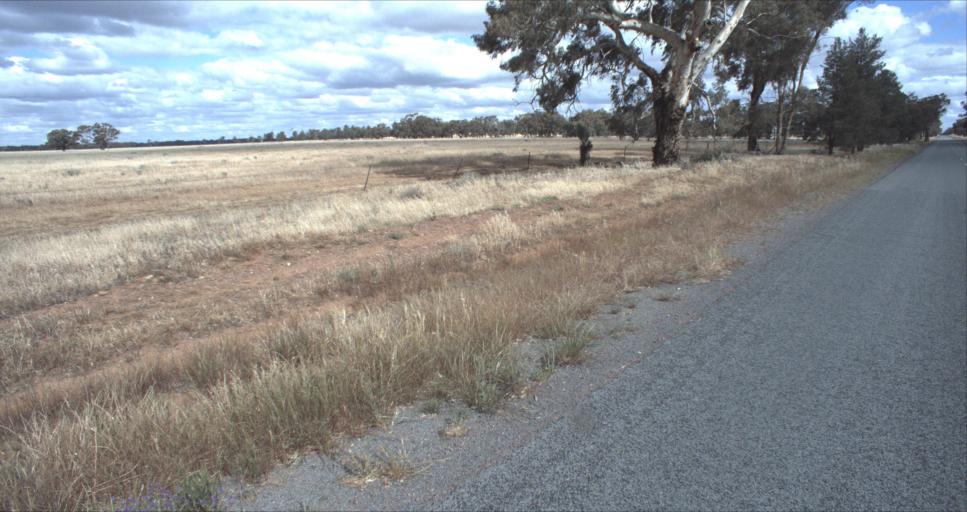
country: AU
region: New South Wales
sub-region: Leeton
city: Leeton
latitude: -34.6653
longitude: 146.3485
